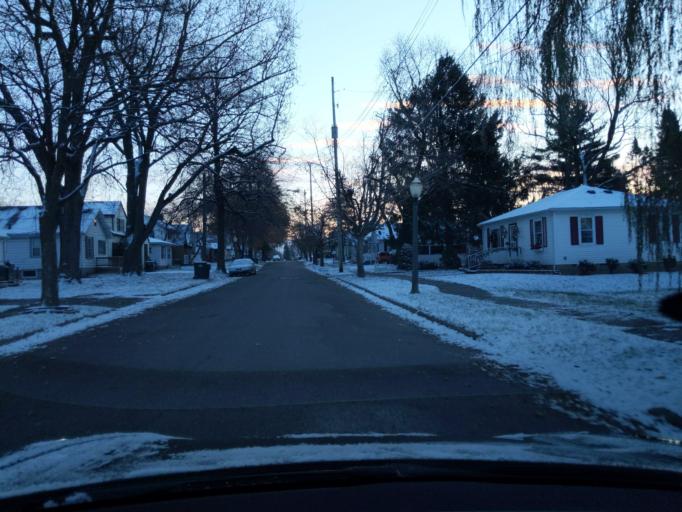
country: US
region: Michigan
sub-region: Ingham County
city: Lansing
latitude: 42.7019
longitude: -84.5509
